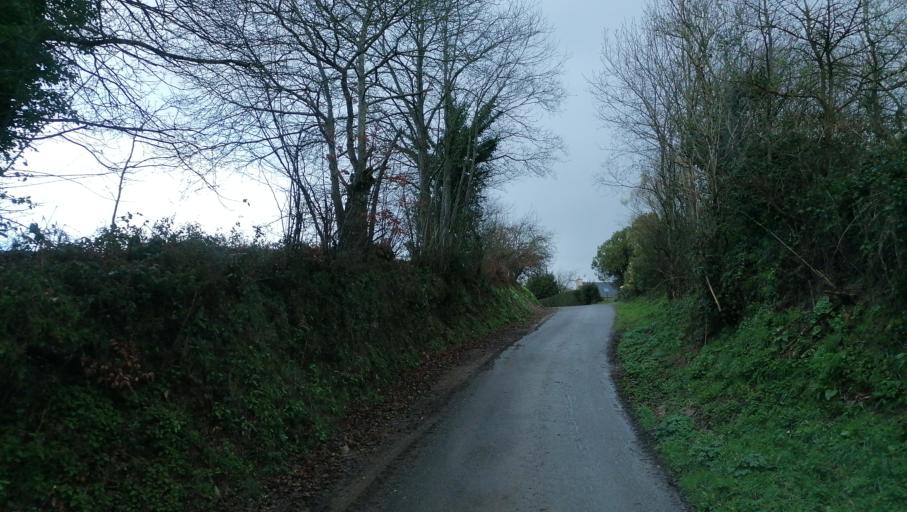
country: FR
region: Brittany
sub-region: Departement des Cotes-d'Armor
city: Plouagat
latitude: 48.4908
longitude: -2.9726
